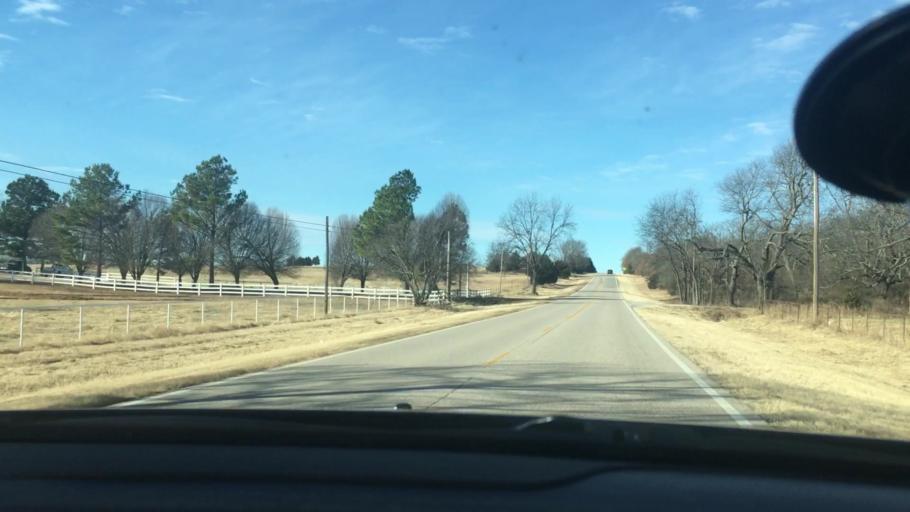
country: US
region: Oklahoma
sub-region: Garvin County
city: Stratford
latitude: 34.9860
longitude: -96.9673
